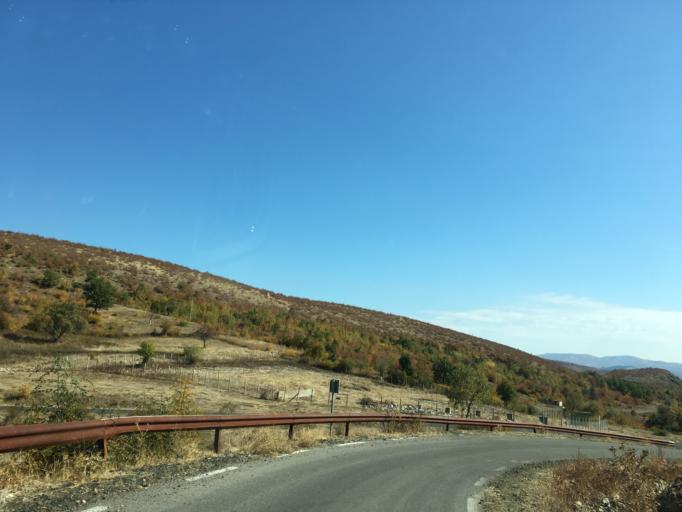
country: BG
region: Kurdzhali
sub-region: Obshtina Krumovgrad
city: Krumovgrad
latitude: 41.5149
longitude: 25.5331
